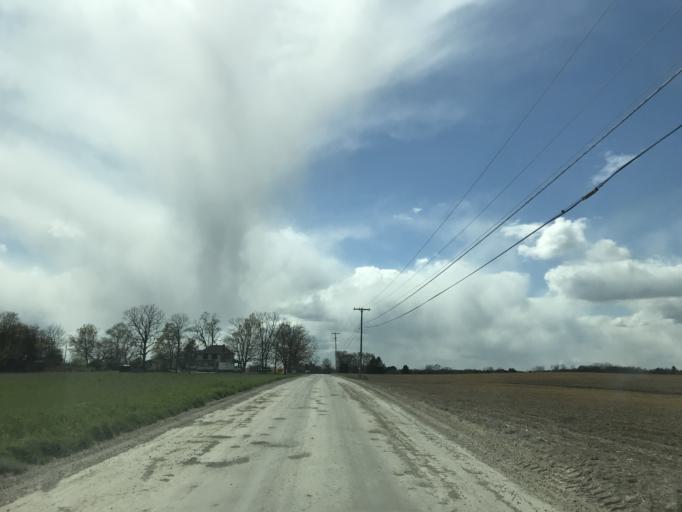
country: US
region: Michigan
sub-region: Oakland County
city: South Lyon
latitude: 42.3883
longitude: -83.6509
